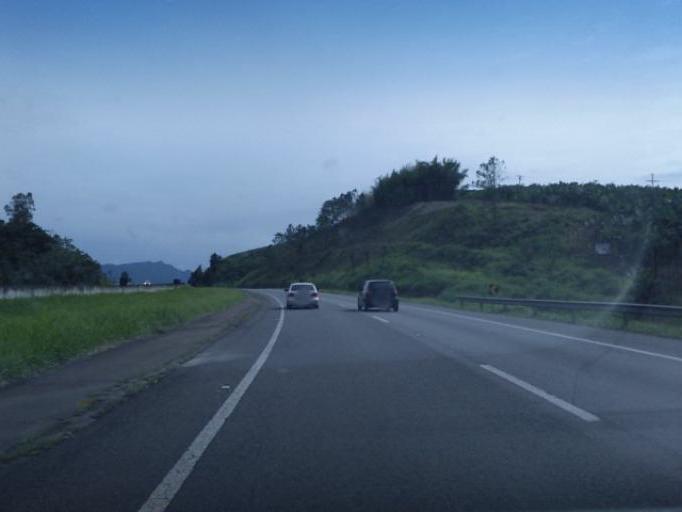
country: BR
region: Sao Paulo
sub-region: Cajati
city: Cajati
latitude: -24.7599
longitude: -48.1651
